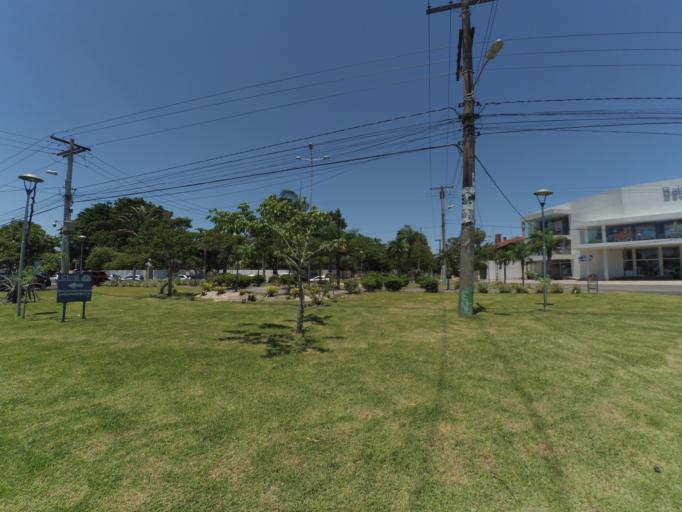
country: BO
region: Santa Cruz
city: Santa Cruz de la Sierra
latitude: -17.7633
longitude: -63.1965
